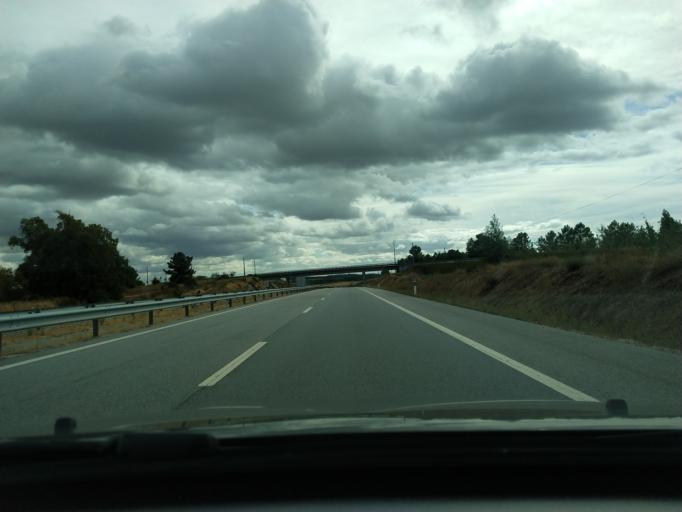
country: PT
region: Guarda
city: Alcains
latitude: 40.0190
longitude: -7.4662
